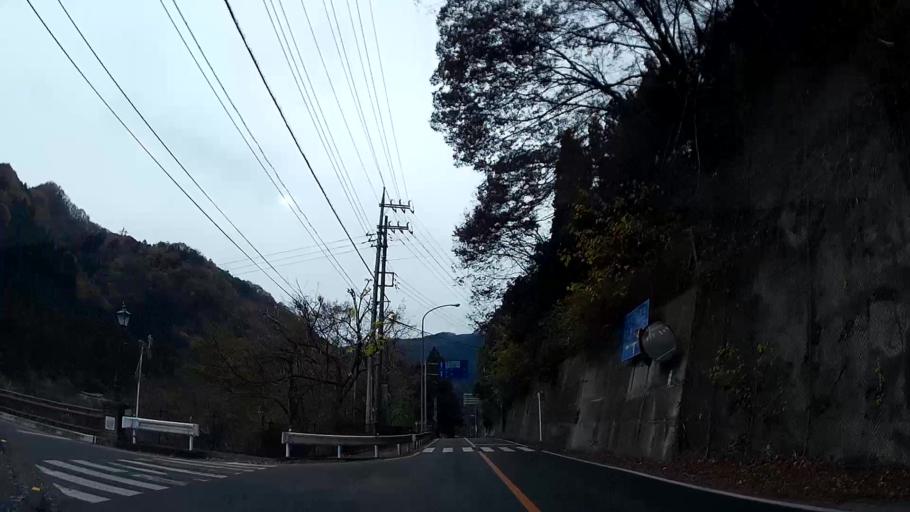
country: JP
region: Saitama
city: Chichibu
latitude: 35.9614
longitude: 138.9742
